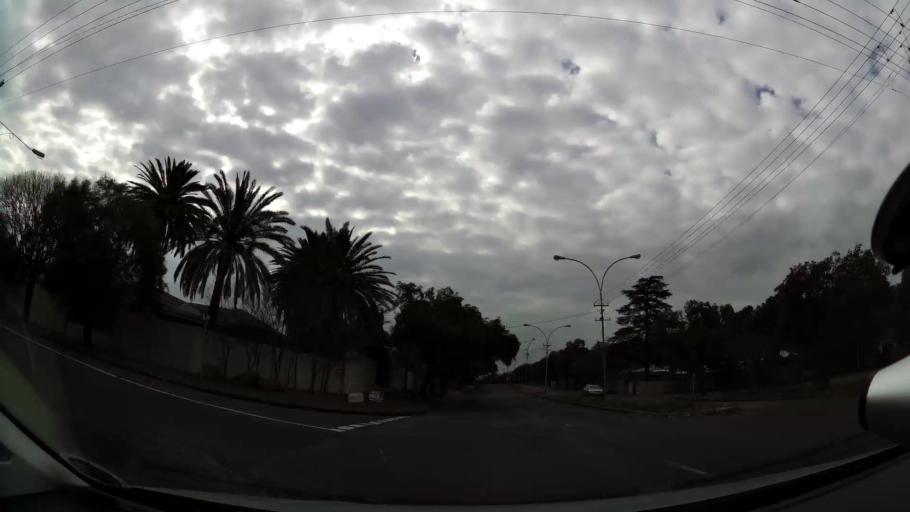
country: ZA
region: Orange Free State
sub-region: Mangaung Metropolitan Municipality
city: Bloemfontein
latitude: -29.0993
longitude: 26.2083
